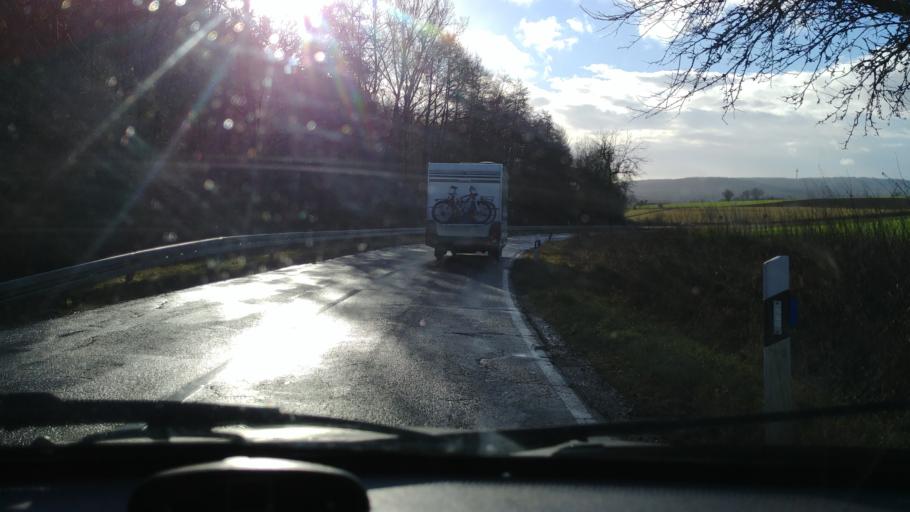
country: DE
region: Hesse
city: Taunusstein
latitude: 50.1620
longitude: 8.1791
